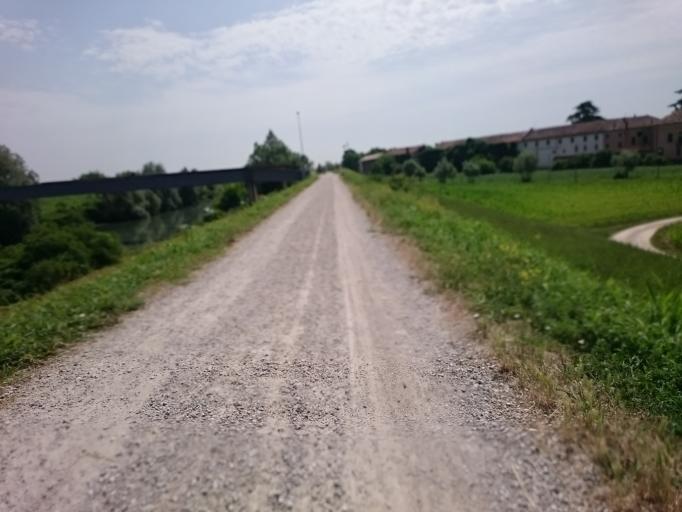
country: IT
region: Veneto
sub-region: Provincia di Padova
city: Correzzola
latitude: 45.2385
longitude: 12.0654
